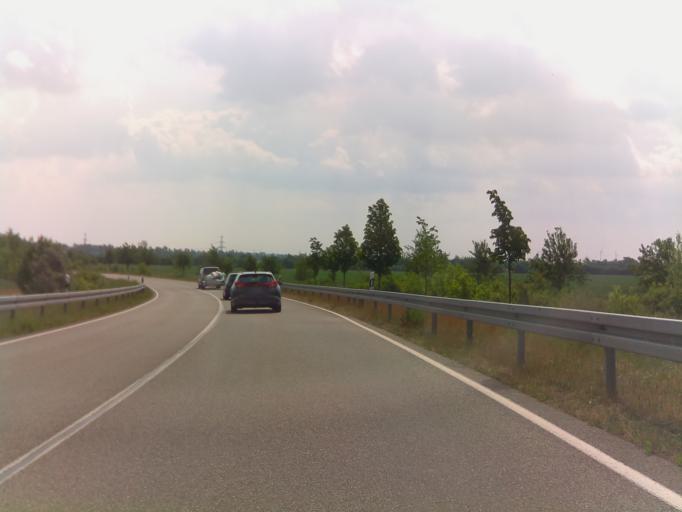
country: DE
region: Saxony-Anhalt
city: Luderitz
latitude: 52.5716
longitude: 11.6960
